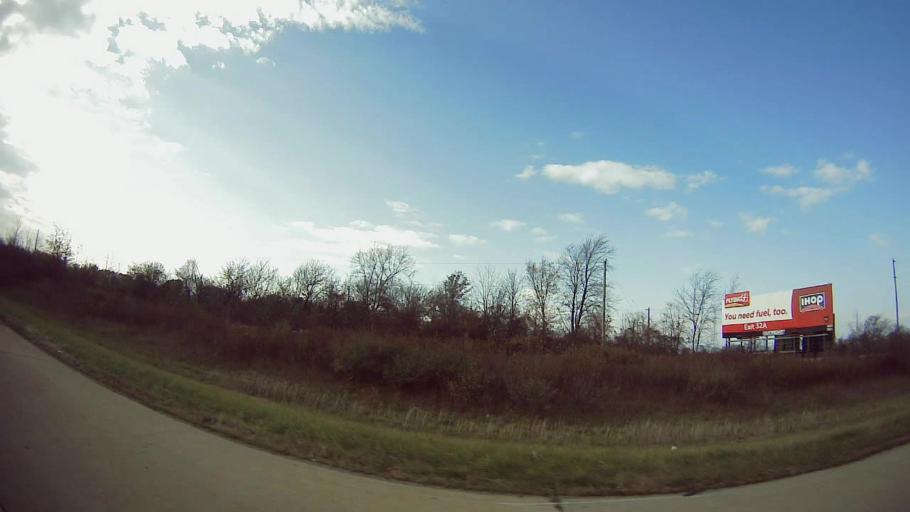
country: US
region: Michigan
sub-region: Monroe County
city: South Rockwood
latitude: 42.0136
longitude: -83.3070
